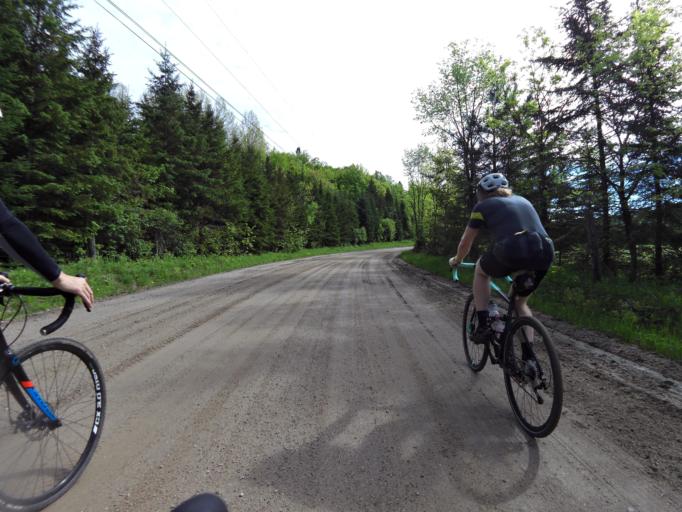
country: CA
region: Quebec
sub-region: Outaouais
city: Wakefield
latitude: 45.7075
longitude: -75.8945
